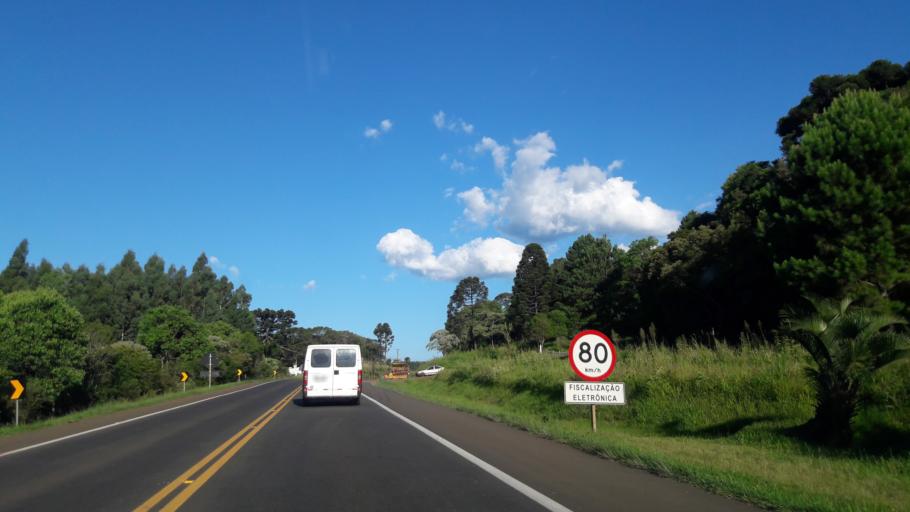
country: BR
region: Parana
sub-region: Guarapuava
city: Guarapuava
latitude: -25.3677
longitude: -51.3377
